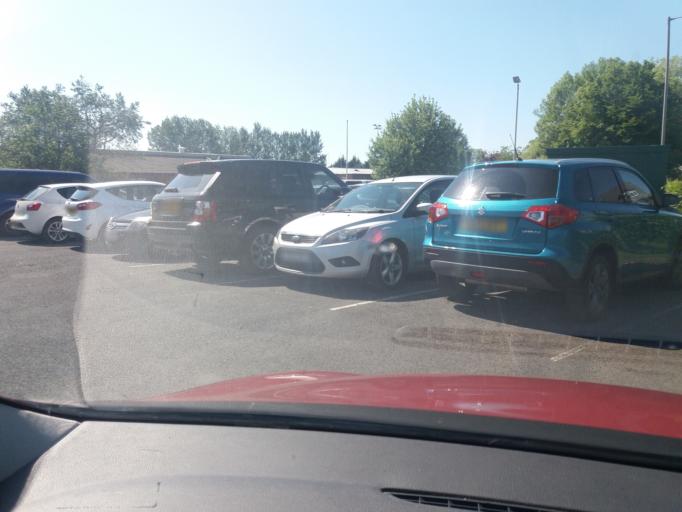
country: GB
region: England
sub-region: Lancashire
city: Preston
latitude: 53.7964
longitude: -2.7316
